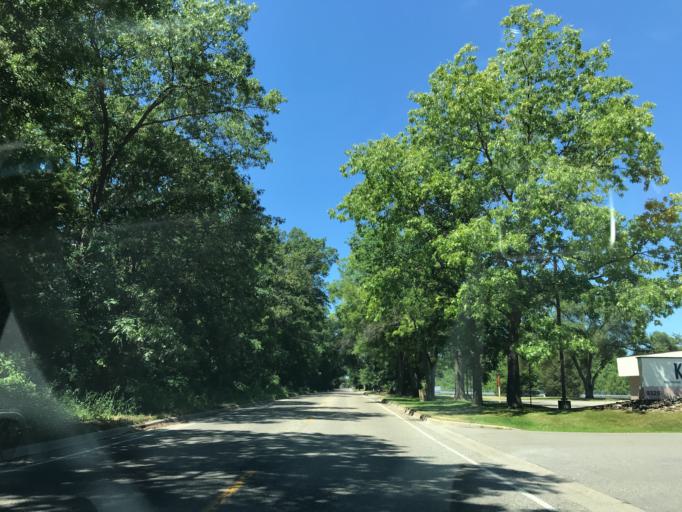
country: US
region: Michigan
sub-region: Livingston County
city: Brighton
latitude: 42.5005
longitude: -83.7604
